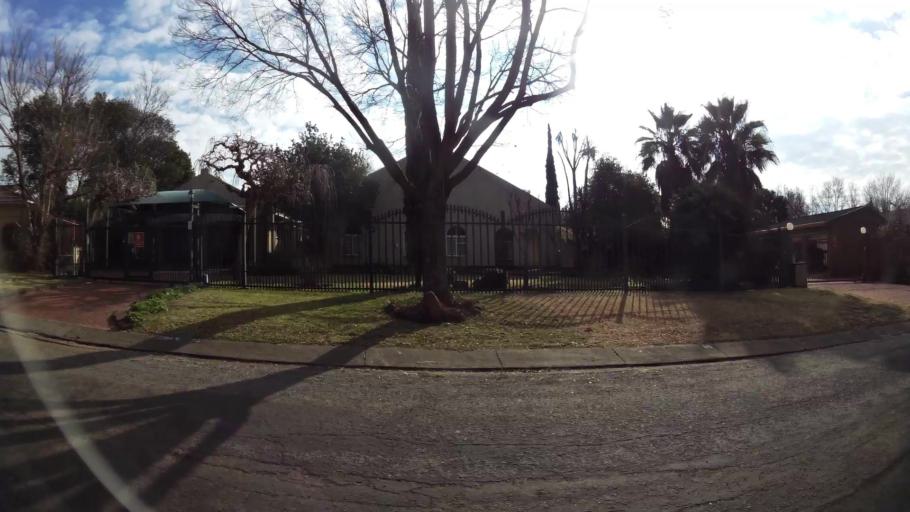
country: ZA
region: Orange Free State
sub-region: Mangaung Metropolitan Municipality
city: Bloemfontein
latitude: -29.0766
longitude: 26.2393
